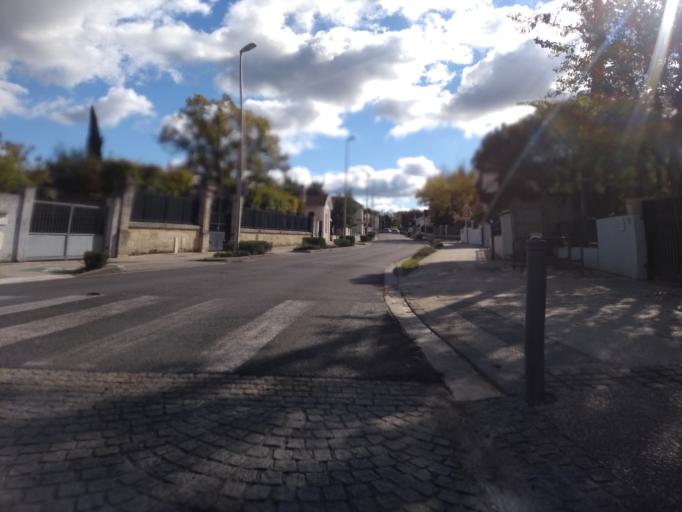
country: FR
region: Aquitaine
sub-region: Departement de la Gironde
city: Pessac
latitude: 44.8018
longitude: -0.6314
